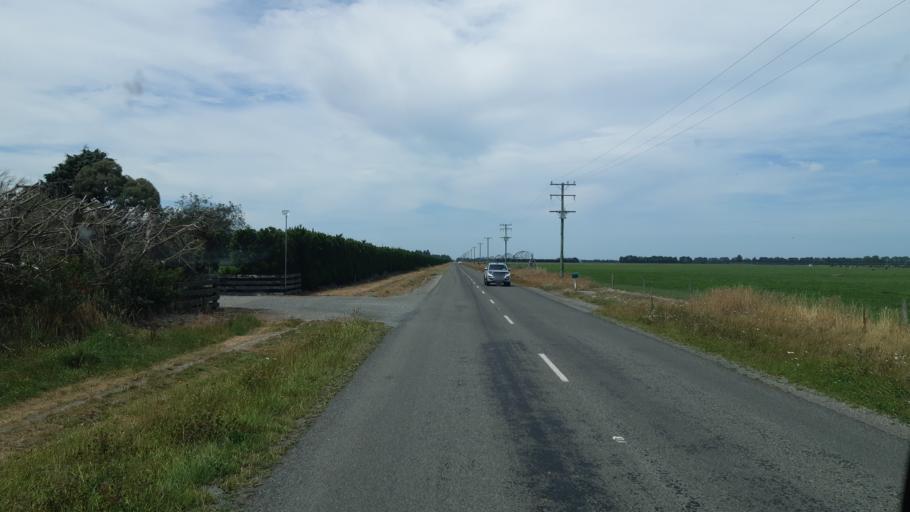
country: NZ
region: Canterbury
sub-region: Ashburton District
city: Tinwald
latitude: -43.9256
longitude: 171.5673
